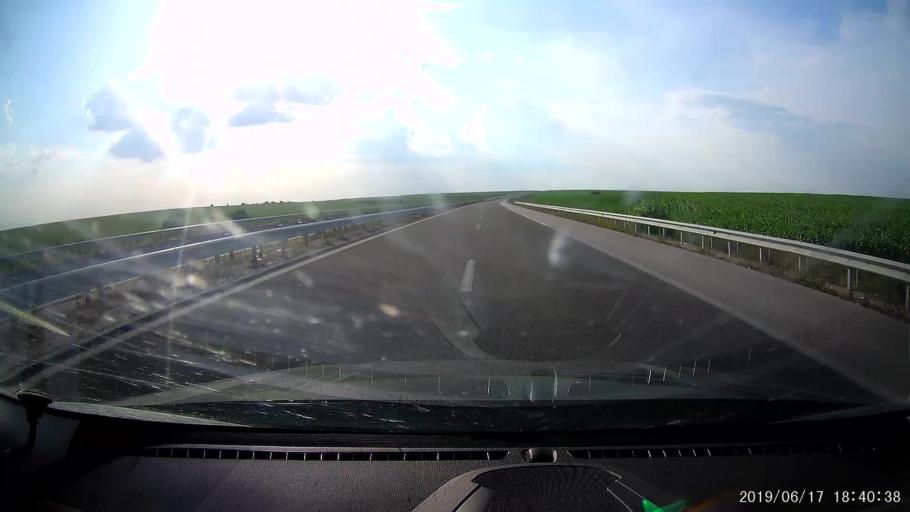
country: BG
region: Stara Zagora
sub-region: Obshtina Chirpan
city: Chirpan
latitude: 42.1581
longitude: 25.2730
